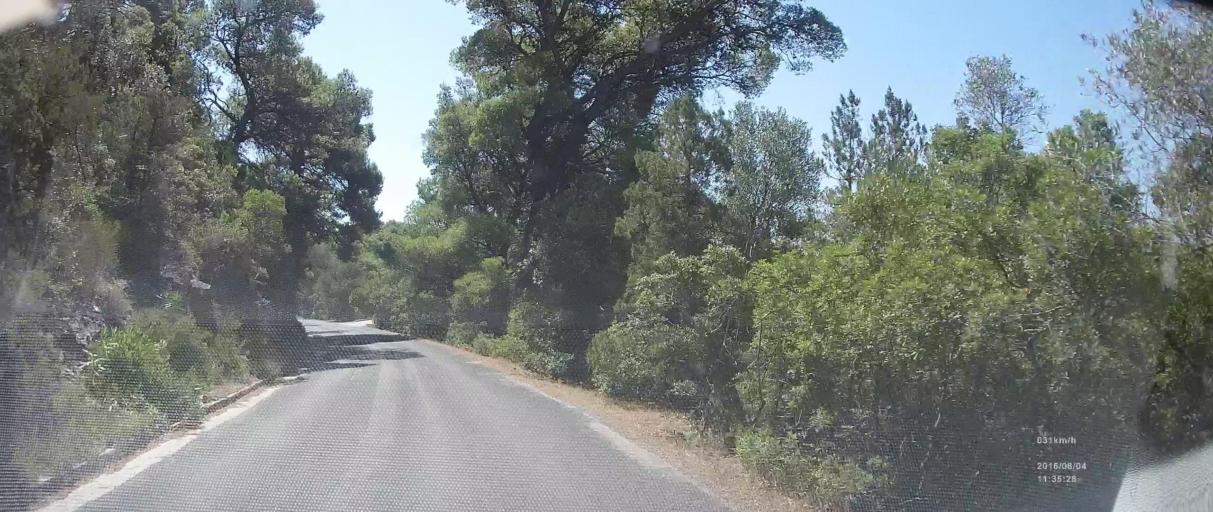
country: HR
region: Dubrovacko-Neretvanska
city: Blato
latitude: 42.7800
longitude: 17.3663
